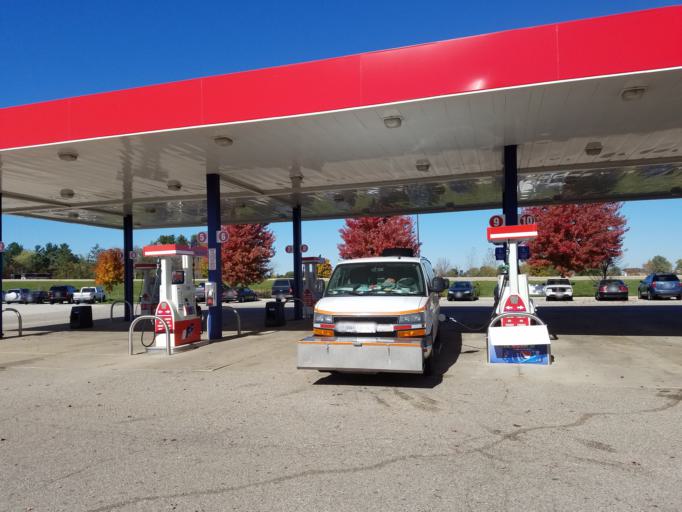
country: US
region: Wisconsin
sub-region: Rock County
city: Beloit
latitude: 42.4904
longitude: -88.9895
